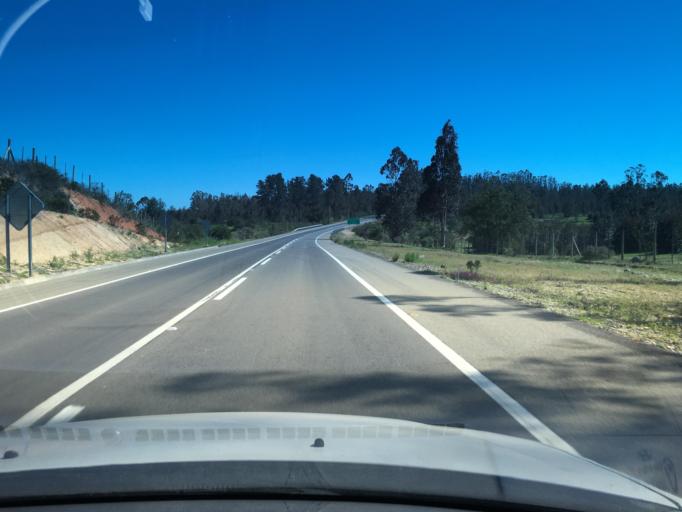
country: CL
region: Valparaiso
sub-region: San Antonio Province
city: El Tabo
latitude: -33.4076
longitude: -71.5495
